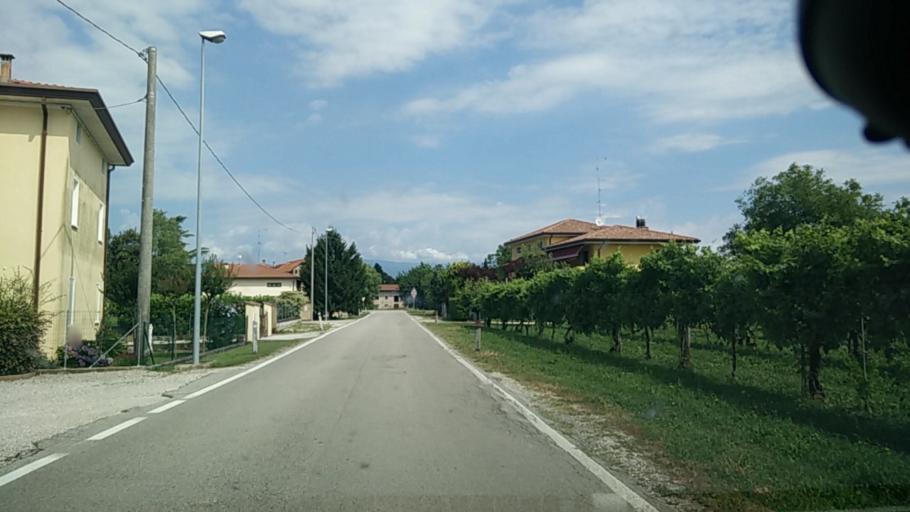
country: IT
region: Veneto
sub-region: Provincia di Treviso
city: Portobuffole
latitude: 45.8573
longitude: 12.5454
